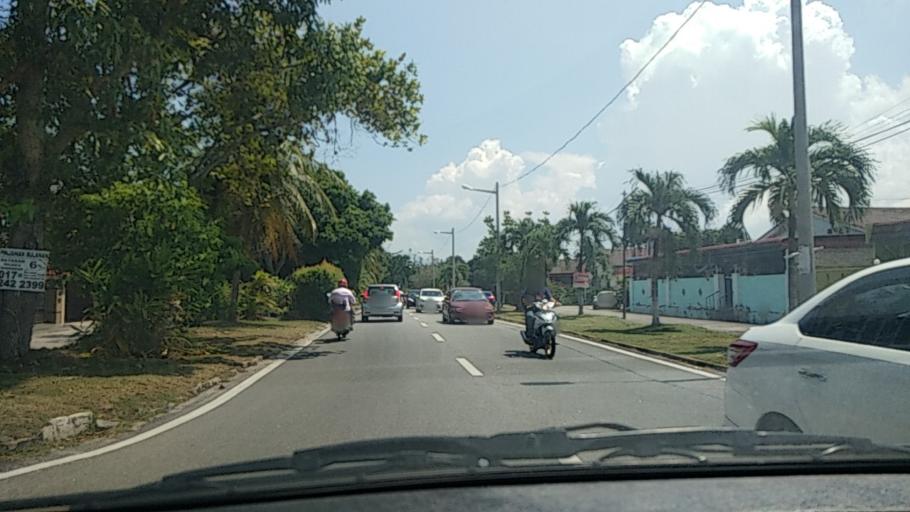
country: MY
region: Kedah
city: Sungai Petani
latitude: 5.6438
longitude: 100.5063
